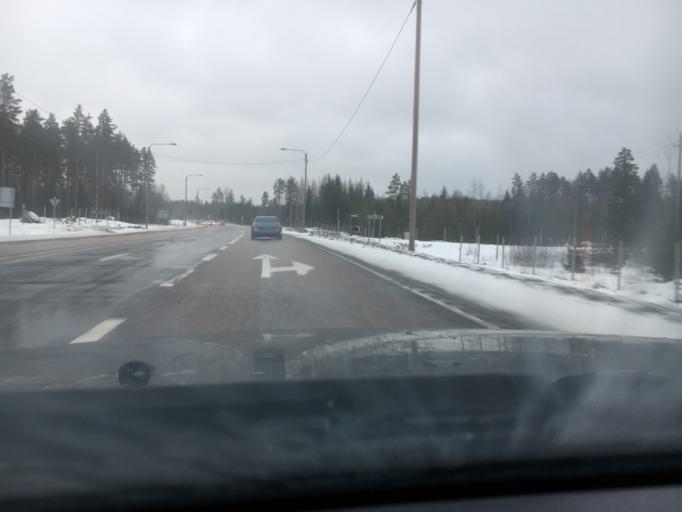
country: FI
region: Central Finland
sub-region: Joutsa
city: Joutsa
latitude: 61.8229
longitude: 26.0976
